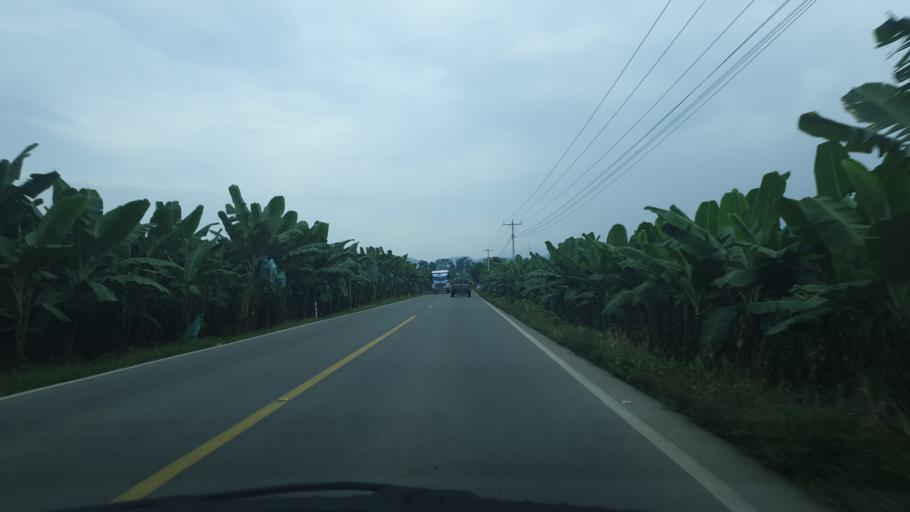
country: EC
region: El Oro
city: Pasaje
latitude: -3.3540
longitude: -79.8206
